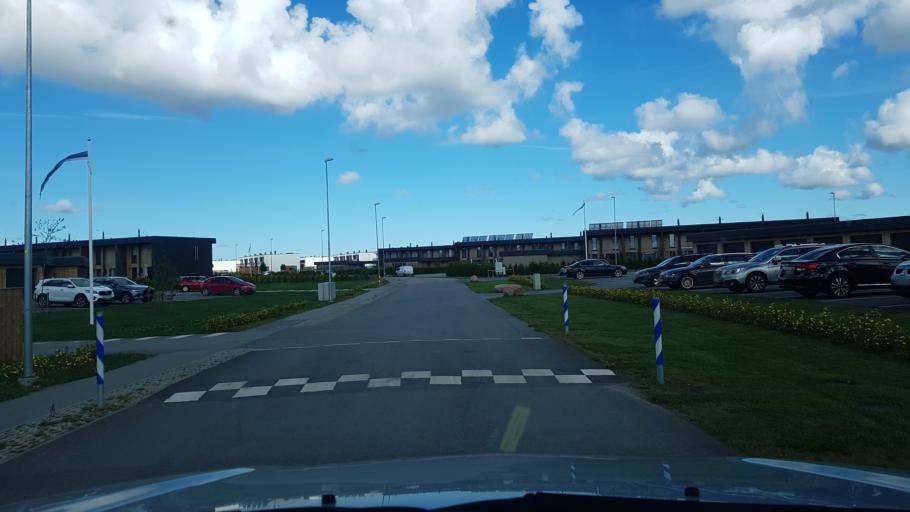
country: EE
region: Harju
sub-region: Tallinna linn
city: Tallinn
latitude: 59.3837
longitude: 24.8090
